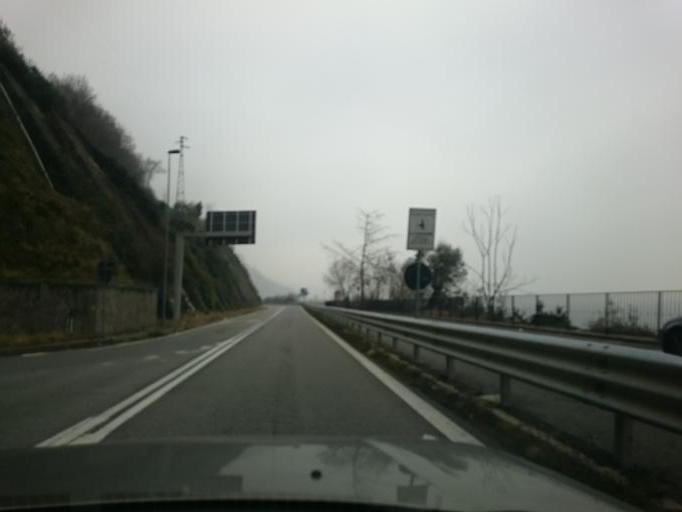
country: IT
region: Lombardy
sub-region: Provincia di Brescia
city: Marone
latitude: 45.7567
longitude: 10.0794
